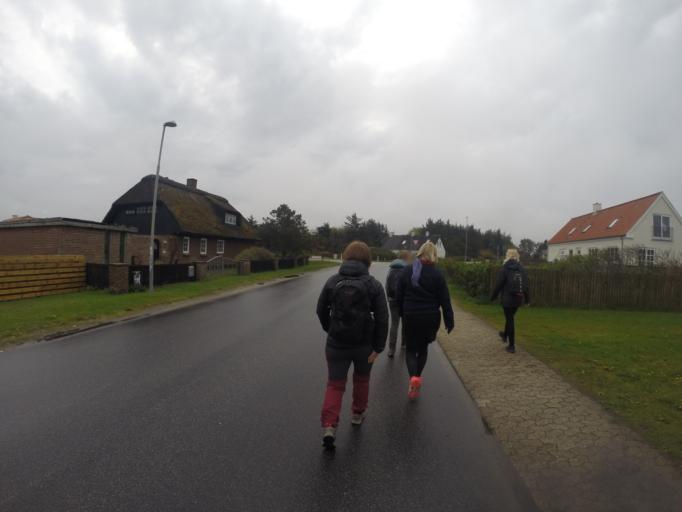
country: DK
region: North Denmark
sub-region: Thisted Kommune
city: Hanstholm
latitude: 57.0406
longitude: 8.5079
